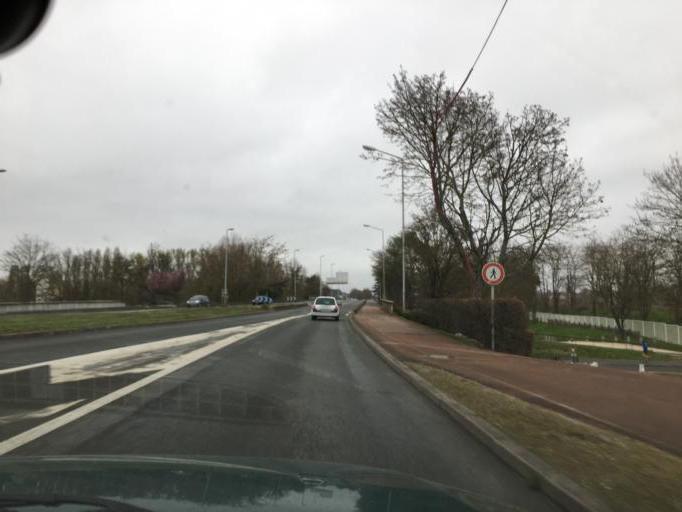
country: FR
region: Centre
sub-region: Departement du Loiret
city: Saint-Jean-le-Blanc
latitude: 47.8928
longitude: 1.9223
